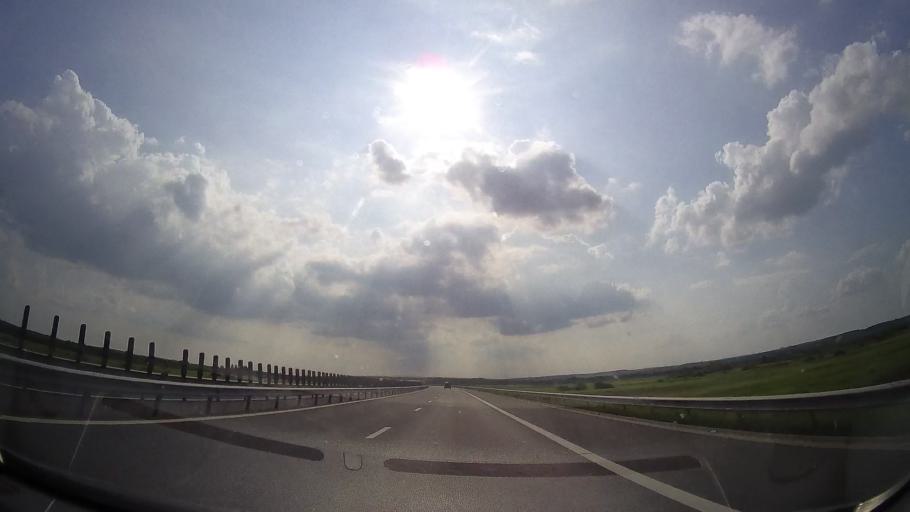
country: RO
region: Timis
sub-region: Comuna Bethausen
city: Bethausen
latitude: 45.8159
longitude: 21.9674
